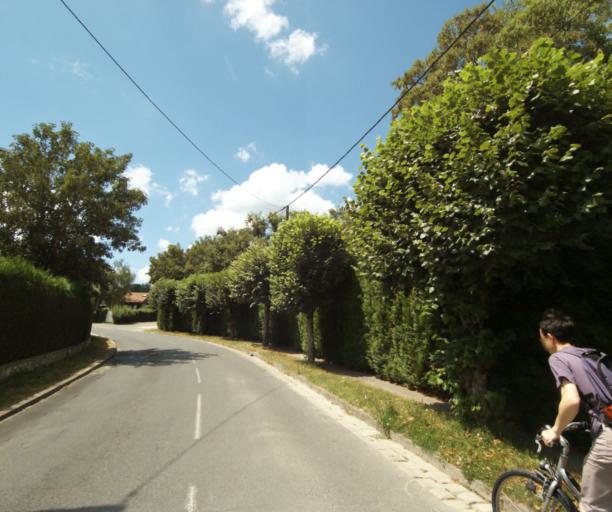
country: FR
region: Ile-de-France
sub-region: Departement de Seine-et-Marne
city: Samois-sur-Seine
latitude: 48.4548
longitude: 2.7582
